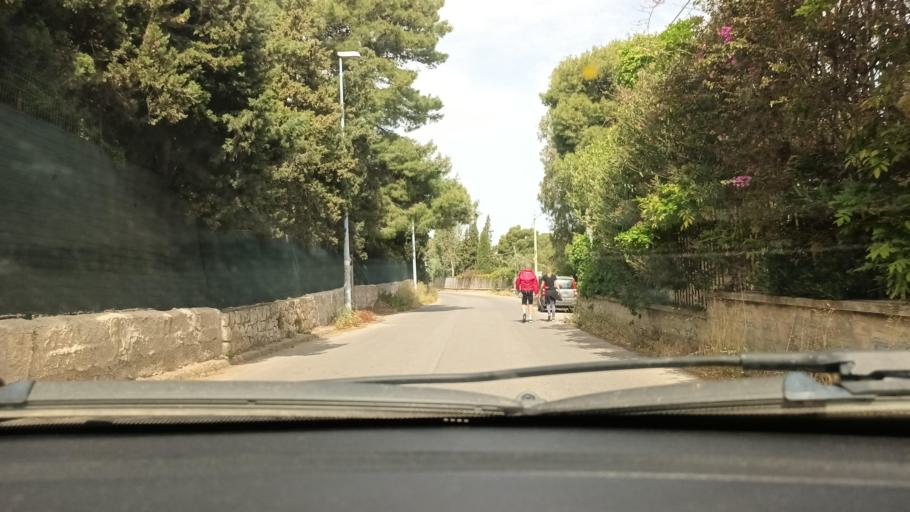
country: IT
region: Sicily
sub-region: Palermo
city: Santa Flavia
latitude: 38.1121
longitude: 13.5263
